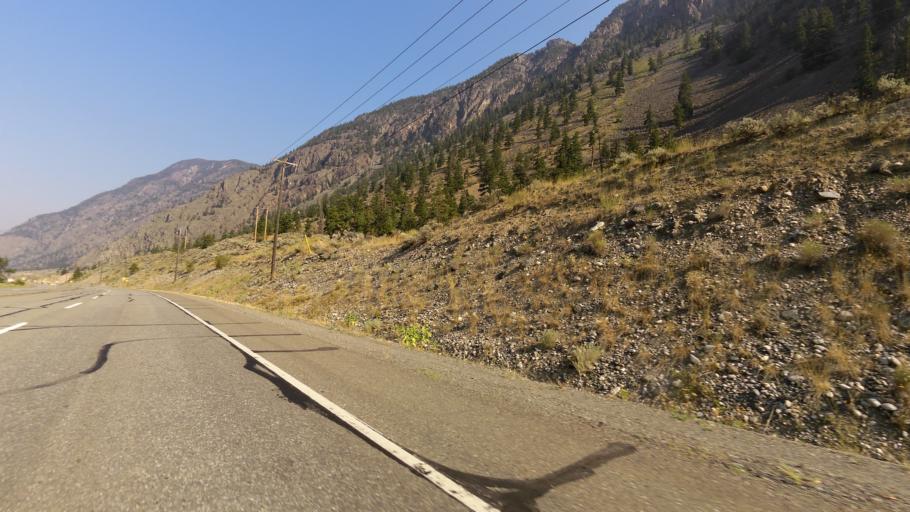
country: CA
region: British Columbia
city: Oliver
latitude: 49.2118
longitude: -119.8977
